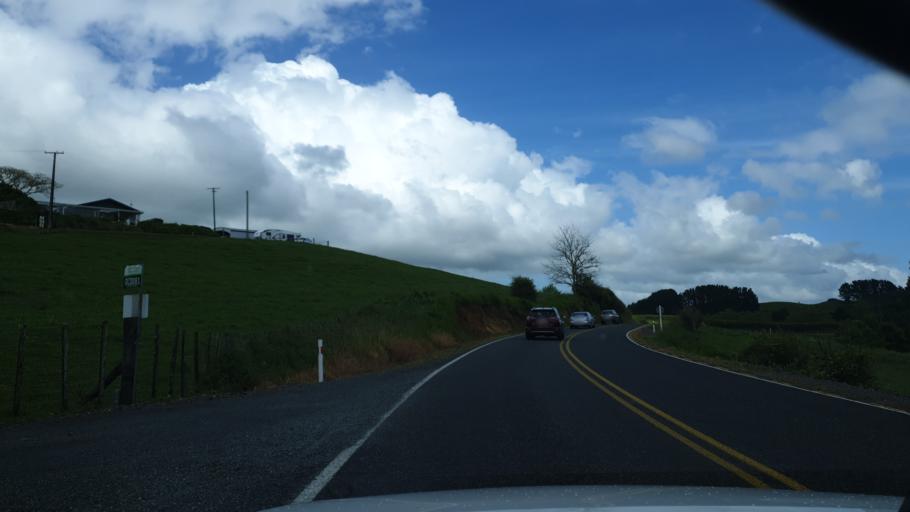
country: NZ
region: Waikato
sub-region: Matamata-Piako District
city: Matamata
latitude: -37.8802
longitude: 175.6974
